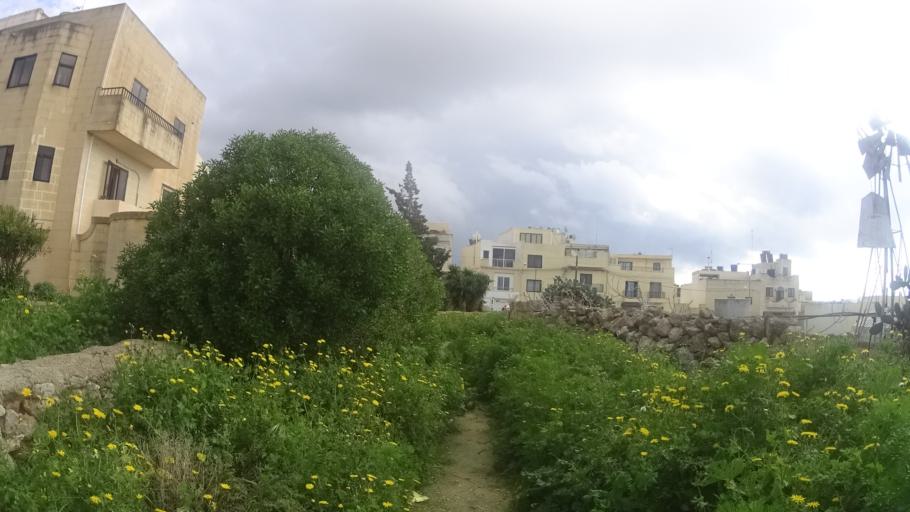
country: MT
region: L-Imtarfa
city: Imtarfa
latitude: 35.8885
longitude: 14.3930
